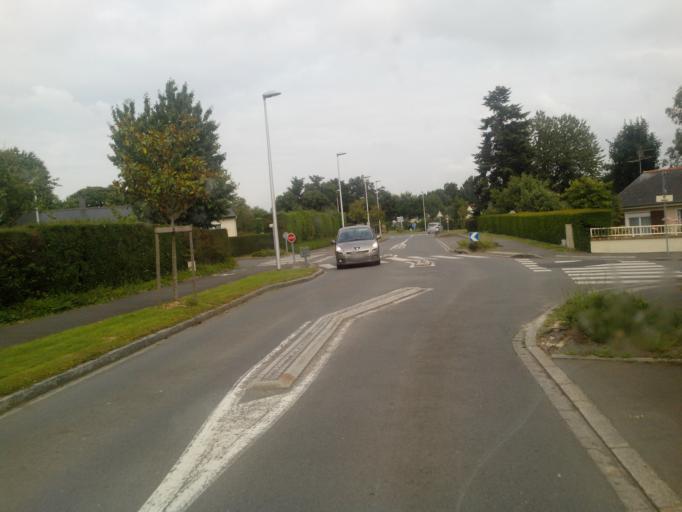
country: FR
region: Brittany
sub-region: Departement d'Ille-et-Vilaine
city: Betton
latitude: 48.1793
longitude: -1.6318
